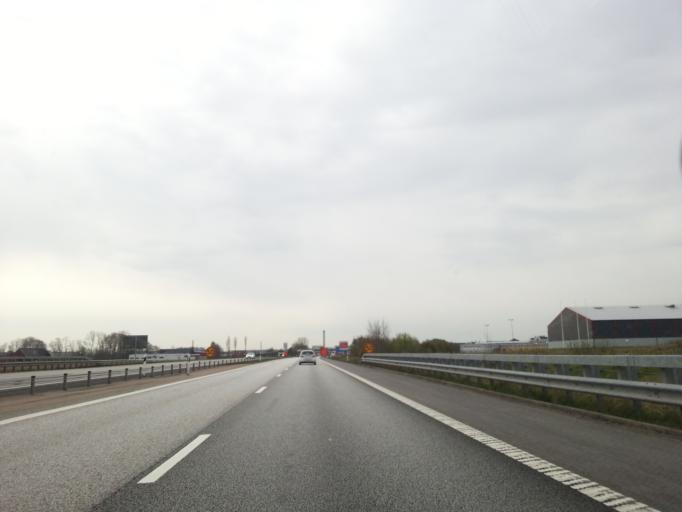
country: SE
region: Skane
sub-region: Angelholms Kommun
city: AEngelholm
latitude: 56.2595
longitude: 12.8959
